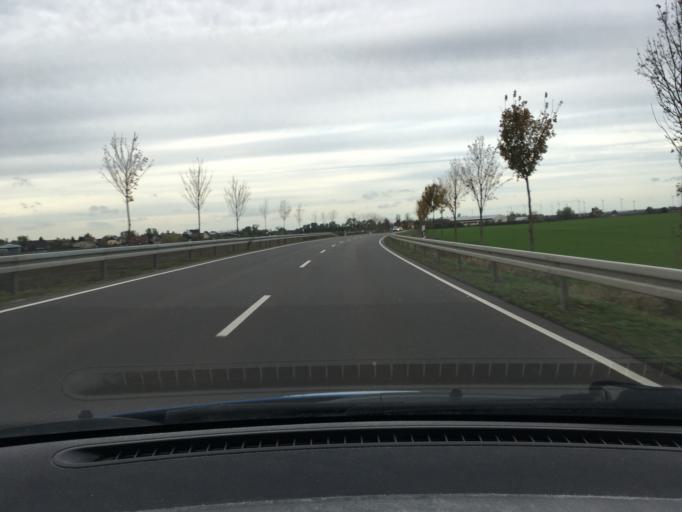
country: DE
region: Saxony-Anhalt
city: Gommern
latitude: 52.0686
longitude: 11.8855
